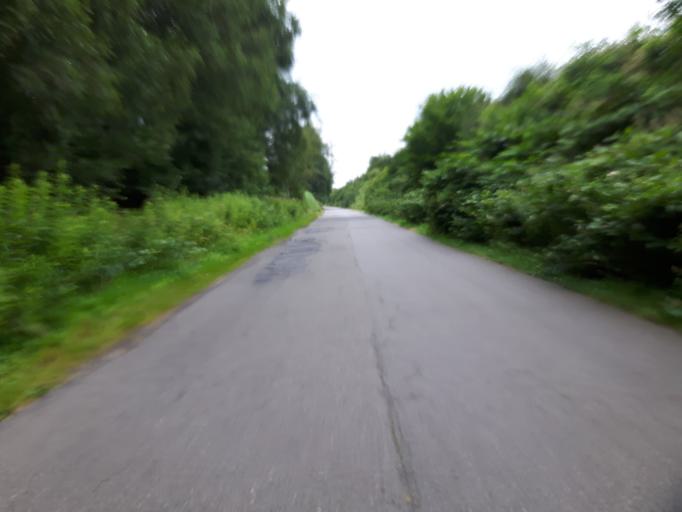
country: DE
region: Lower Saxony
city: Stelle
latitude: 53.3994
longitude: 10.0743
